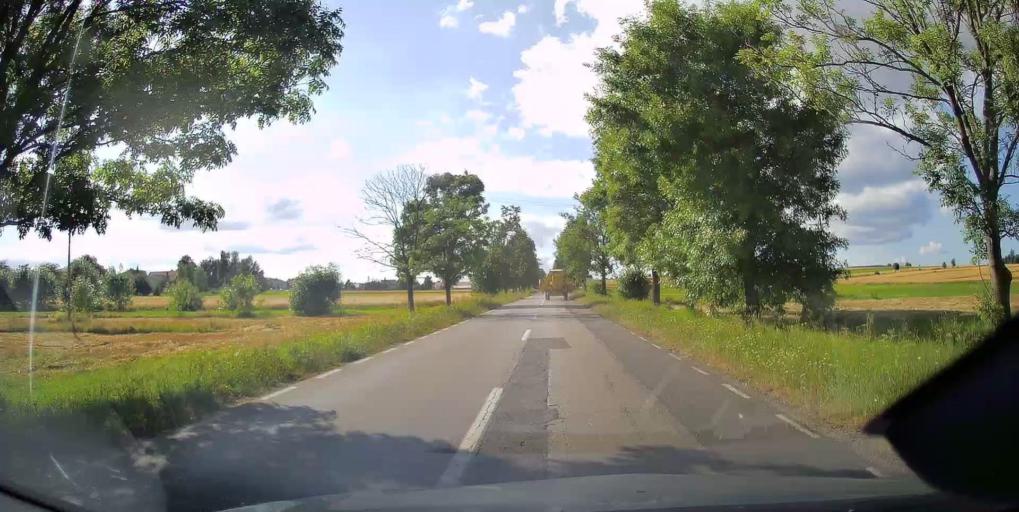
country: PL
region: Swietokrzyskie
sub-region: Powiat kielecki
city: Bodzentyn
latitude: 50.9623
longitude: 20.9007
